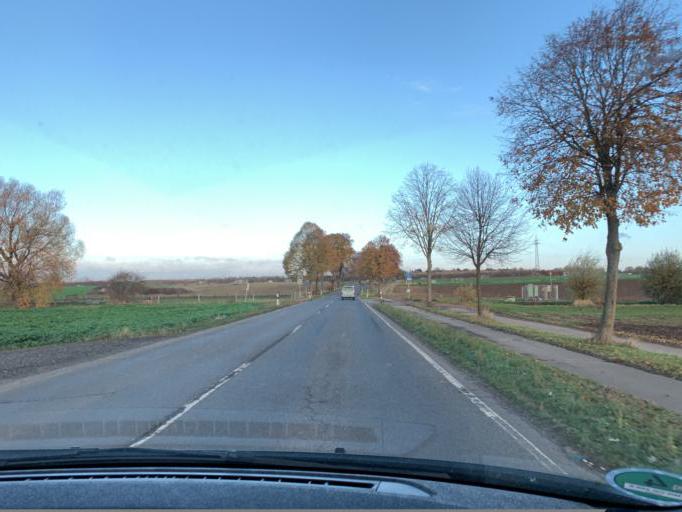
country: DE
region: North Rhine-Westphalia
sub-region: Regierungsbezirk Koln
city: Titz
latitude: 51.0853
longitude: 6.4190
